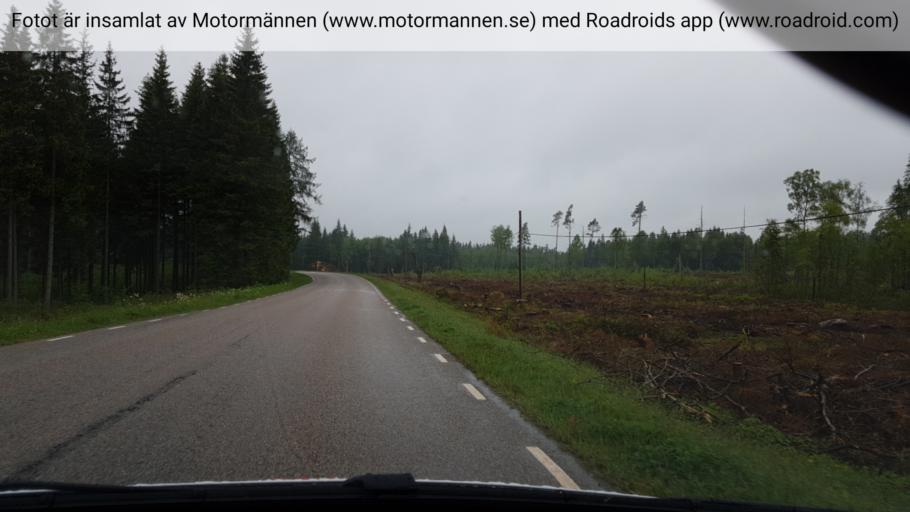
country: SE
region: Vaestra Goetaland
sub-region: Ulricehamns Kommun
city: Ulricehamn
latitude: 57.8029
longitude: 13.5639
